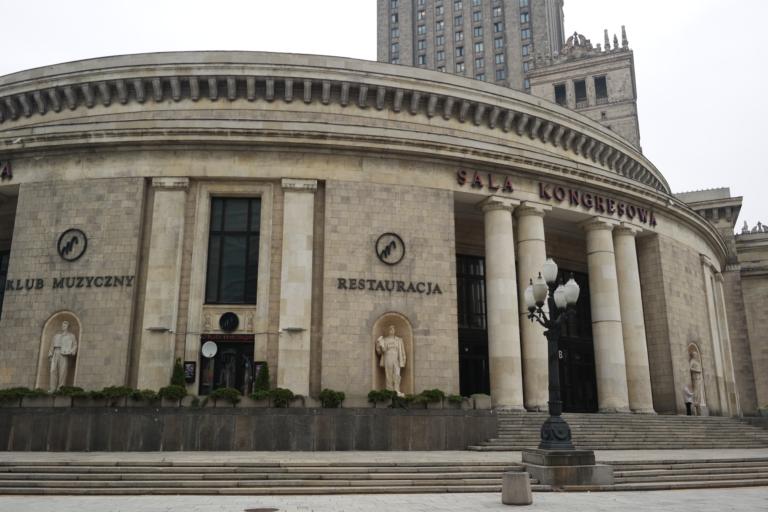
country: PL
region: Masovian Voivodeship
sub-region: Warszawa
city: Warsaw
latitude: 52.2314
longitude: 21.0040
